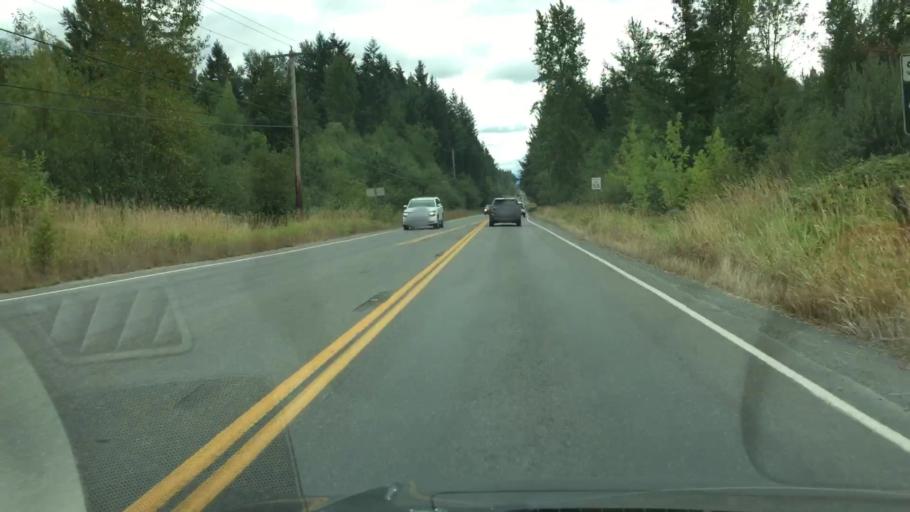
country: US
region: Washington
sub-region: Pierce County
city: Graham
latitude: 46.9793
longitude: -122.2980
